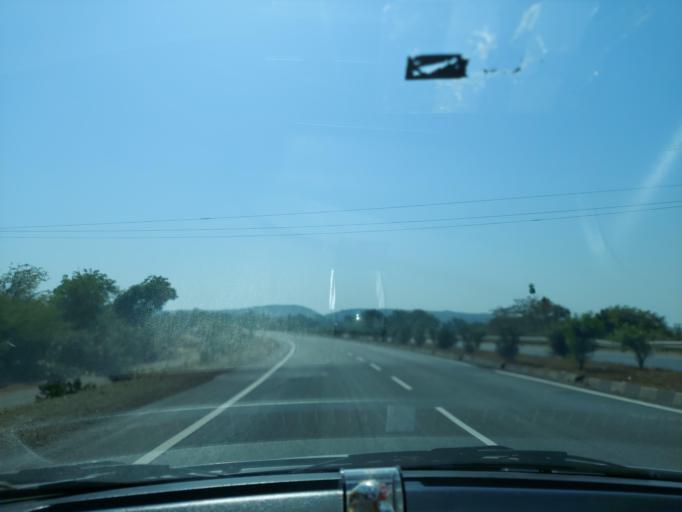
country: IN
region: Madhya Pradesh
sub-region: Dhar
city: Dhamnod
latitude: 22.3244
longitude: 75.4964
